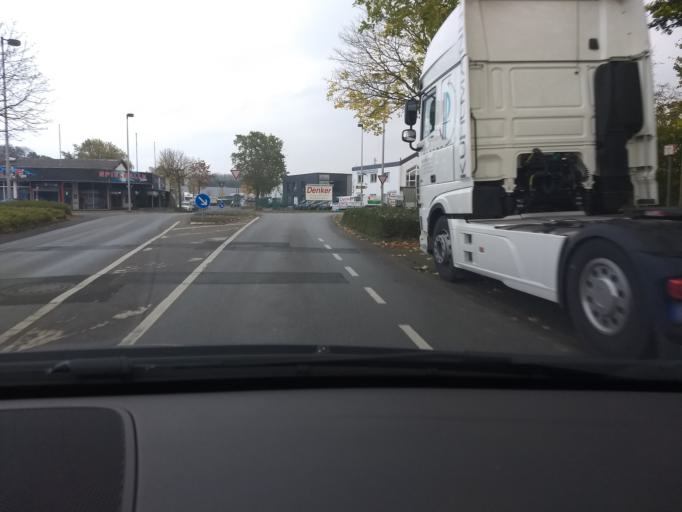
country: DE
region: North Rhine-Westphalia
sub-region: Regierungsbezirk Munster
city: Borken
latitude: 51.8570
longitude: 6.8754
